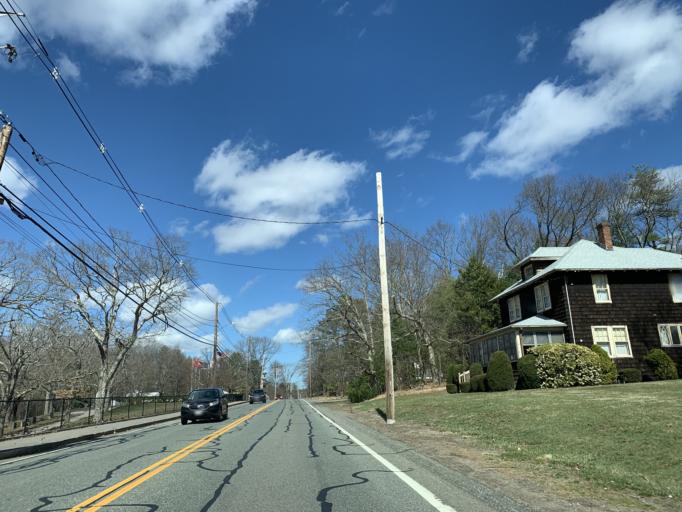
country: US
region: Massachusetts
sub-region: Norfolk County
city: Canton
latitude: 42.1791
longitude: -71.1292
